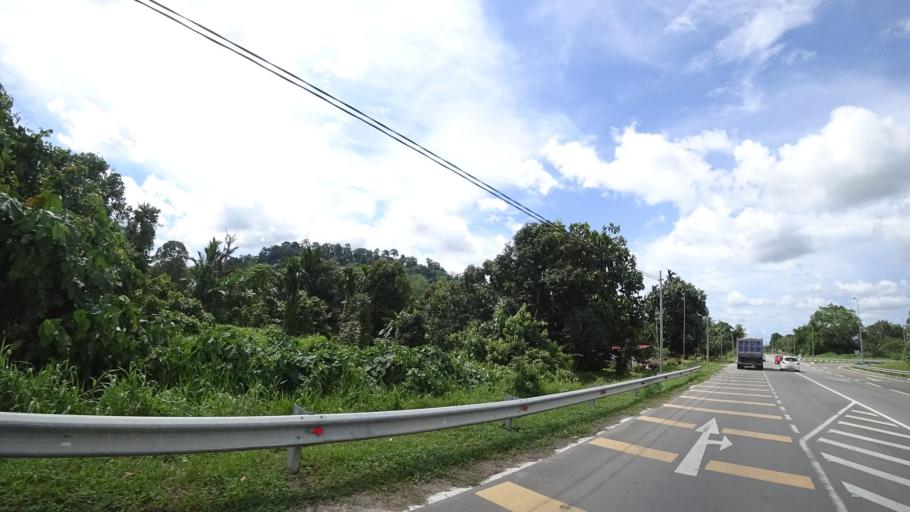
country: BN
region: Tutong
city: Tutong
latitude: 4.7497
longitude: 114.8162
